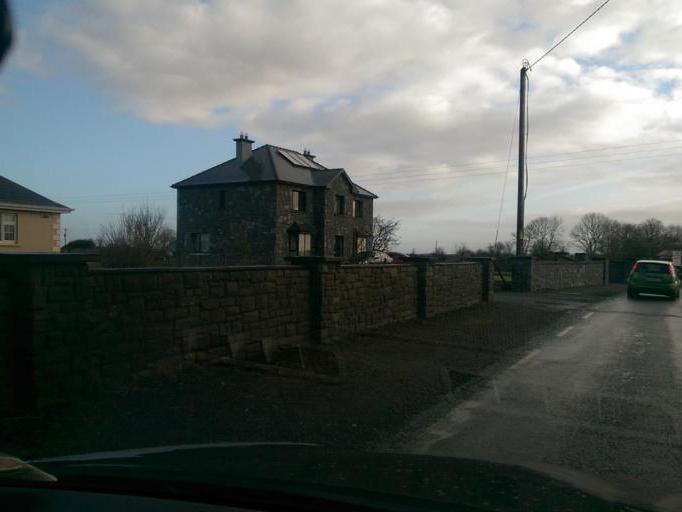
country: IE
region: Connaught
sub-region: County Galway
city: Oranmore
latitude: 53.3121
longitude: -8.8926
